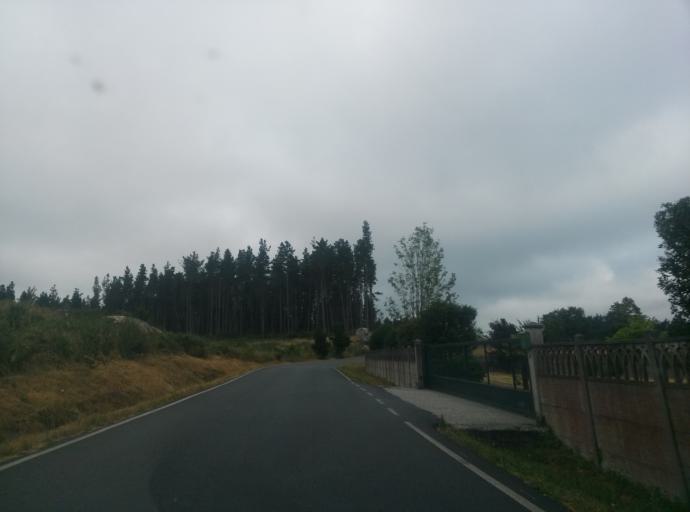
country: ES
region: Galicia
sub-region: Provincia de Lugo
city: Lugo
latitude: 43.0719
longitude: -7.5555
